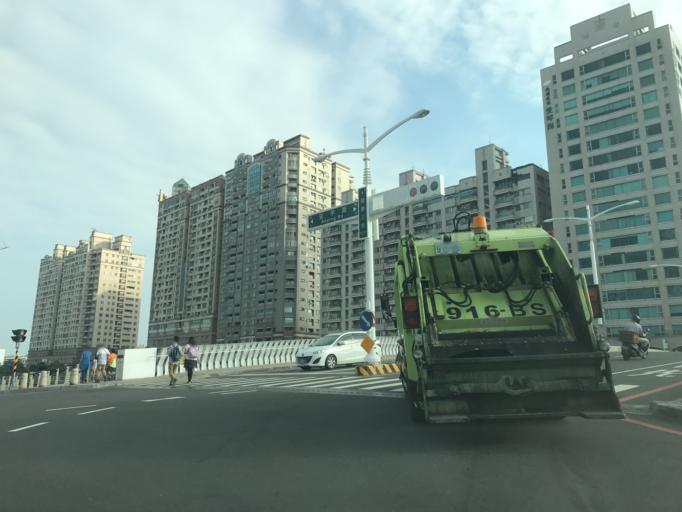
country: TW
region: Taiwan
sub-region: Tainan
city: Tainan
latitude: 22.9986
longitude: 120.1697
